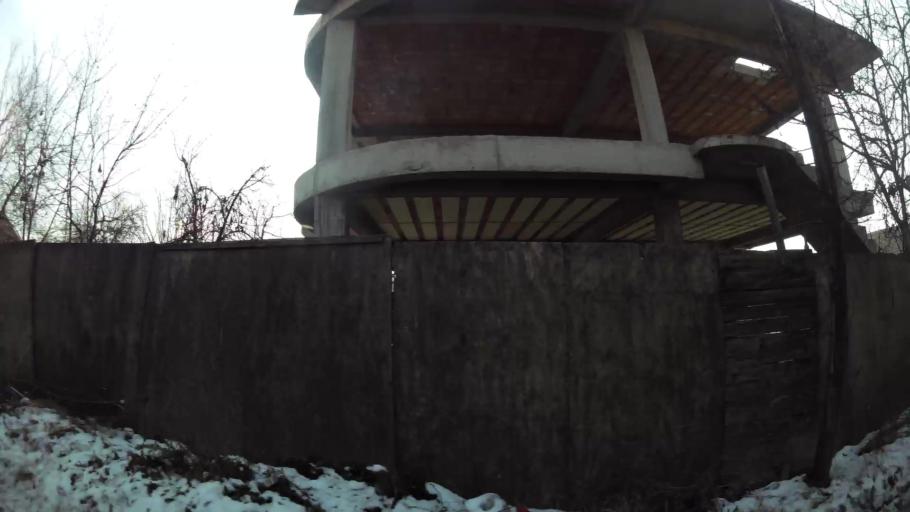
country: MK
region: Kisela Voda
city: Kisela Voda
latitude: 41.9965
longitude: 21.4965
